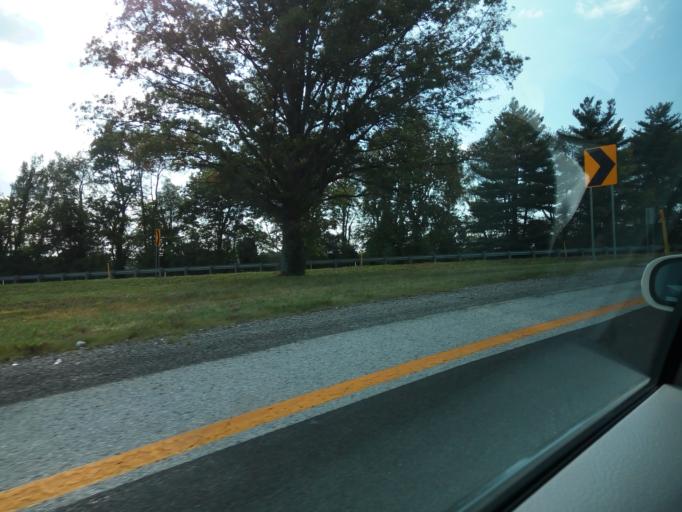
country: US
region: Kentucky
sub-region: Jefferson County
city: Worthington
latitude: 38.3143
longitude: -85.5847
